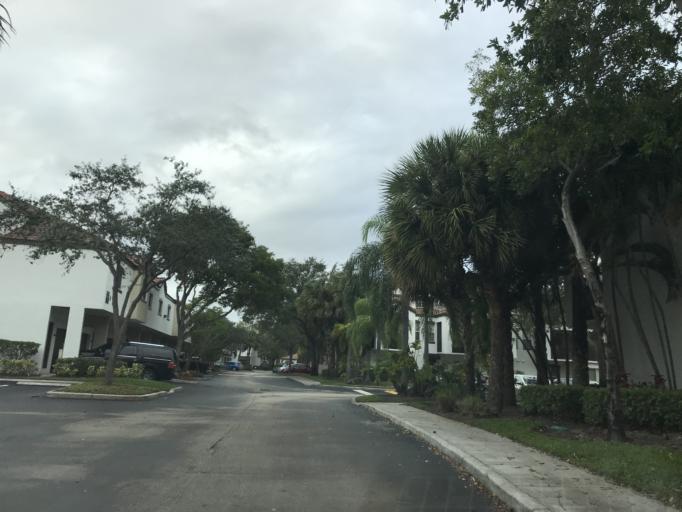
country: US
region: Florida
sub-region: Broward County
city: Coral Springs
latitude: 26.2984
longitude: -80.2804
